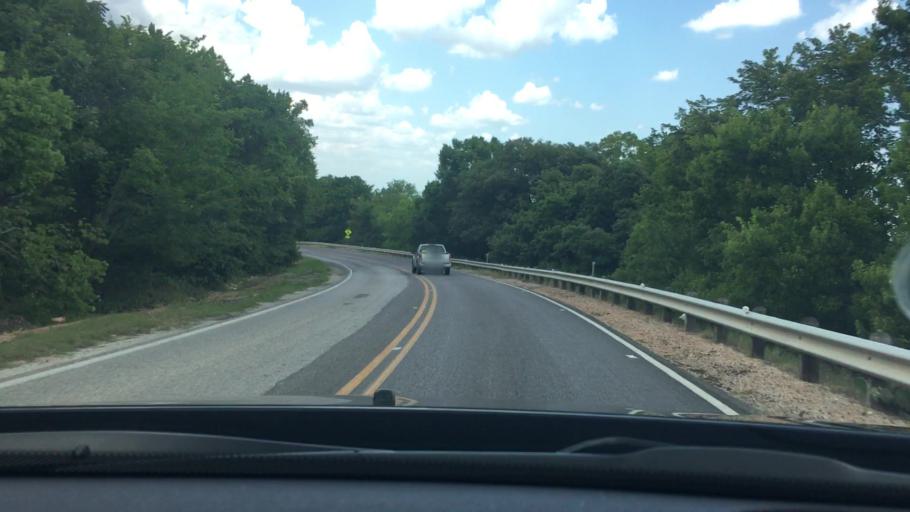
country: US
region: Oklahoma
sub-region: Pontotoc County
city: Ada
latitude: 34.5711
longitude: -96.6287
